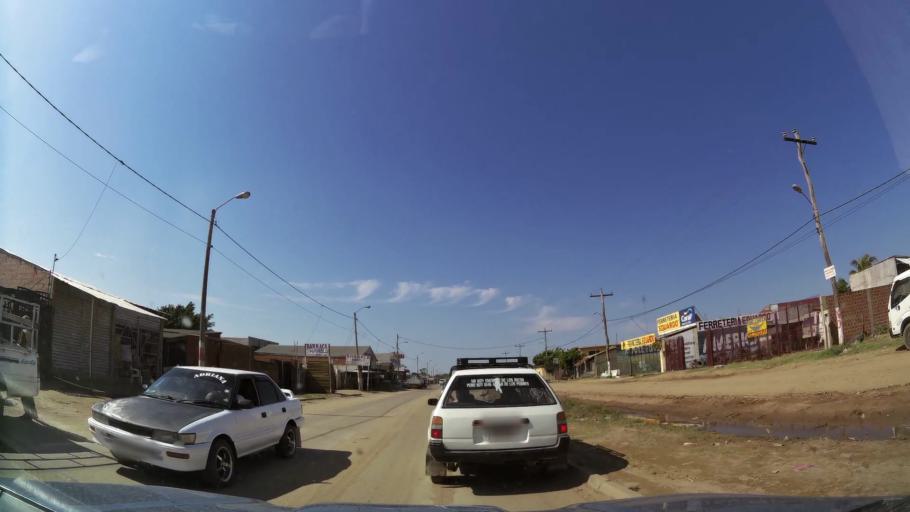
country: BO
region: Santa Cruz
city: Cotoca
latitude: -17.7319
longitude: -63.0960
